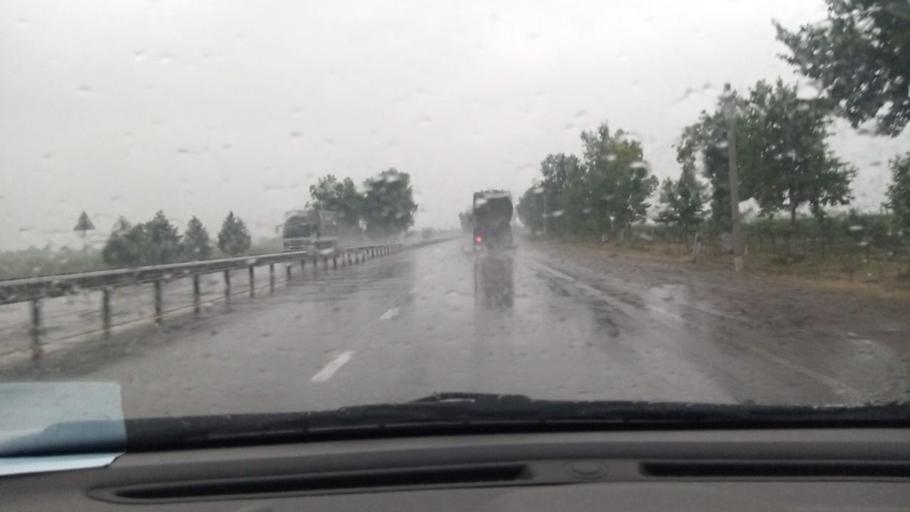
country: UZ
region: Toshkent Shahri
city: Bektemir
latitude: 41.1469
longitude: 69.4298
